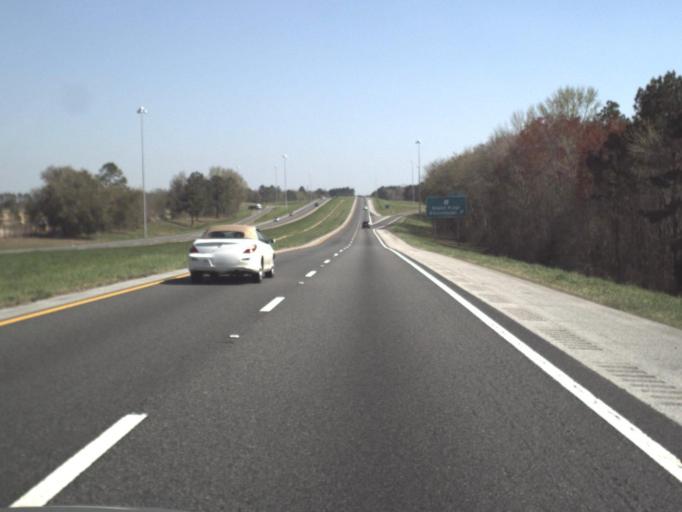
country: US
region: Florida
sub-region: Jackson County
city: Sneads
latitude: 30.6612
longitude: -85.0458
